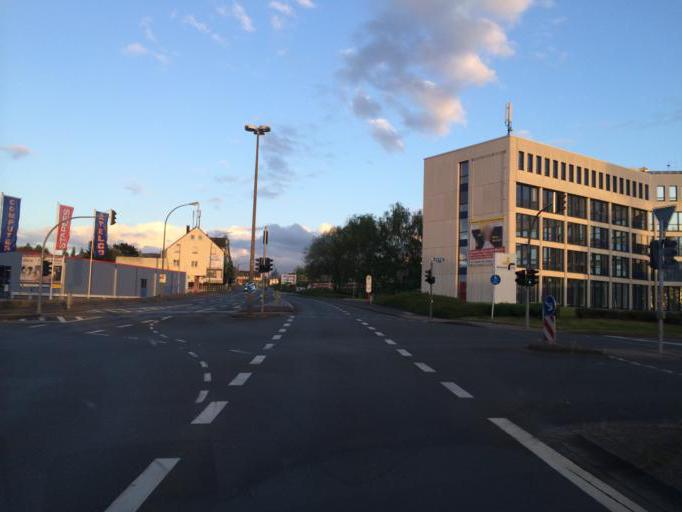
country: DE
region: North Rhine-Westphalia
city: Witten
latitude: 51.4916
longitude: 7.3715
